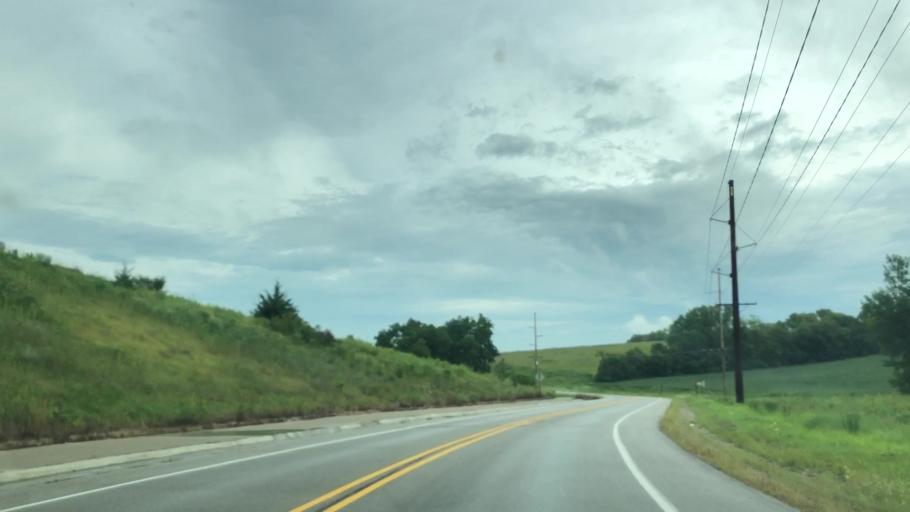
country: US
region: Iowa
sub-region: Marshall County
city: Marshalltown
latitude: 42.0082
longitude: -92.9613
